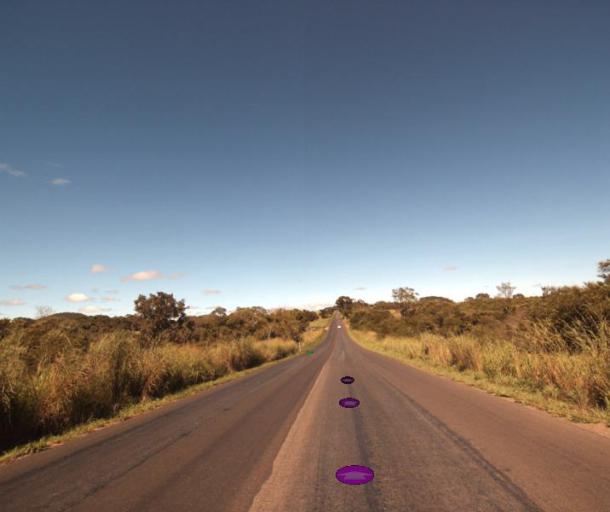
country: BR
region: Goias
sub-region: Itapaci
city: Itapaci
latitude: -15.1334
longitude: -49.5167
